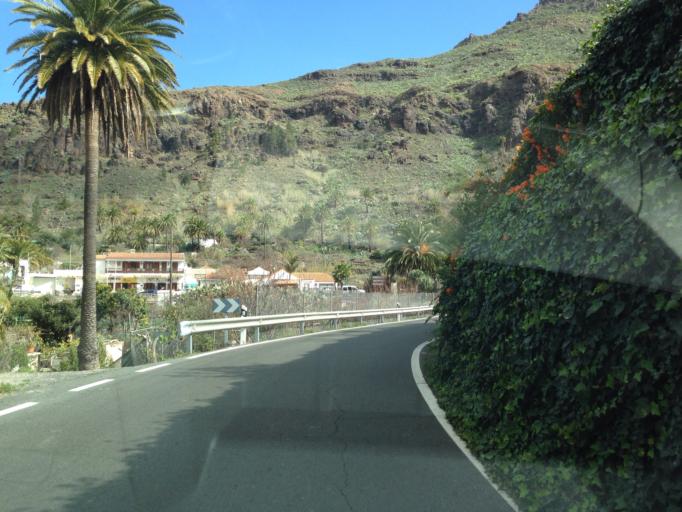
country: ES
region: Canary Islands
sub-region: Provincia de Las Palmas
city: Santa Lucia
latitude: 27.8853
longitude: -15.5643
